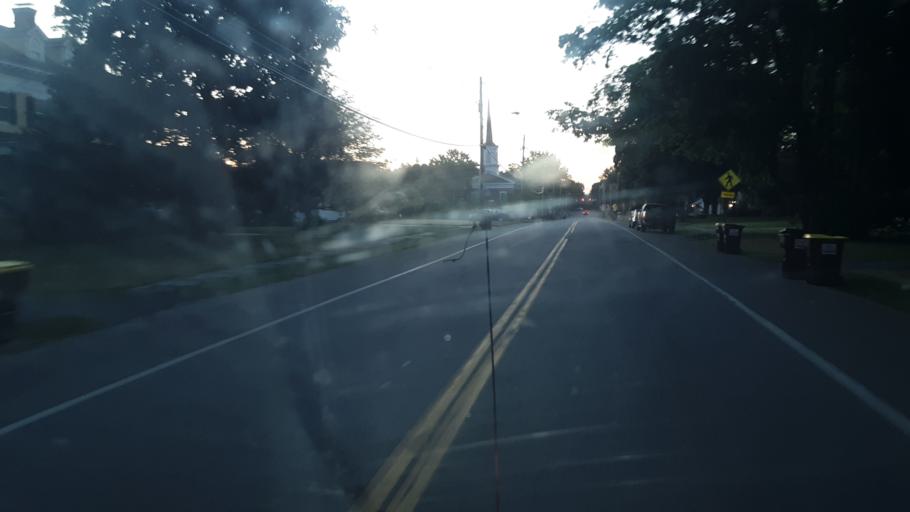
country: US
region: New York
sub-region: Saratoga County
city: Ballston Spa
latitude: 43.0005
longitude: -73.8532
